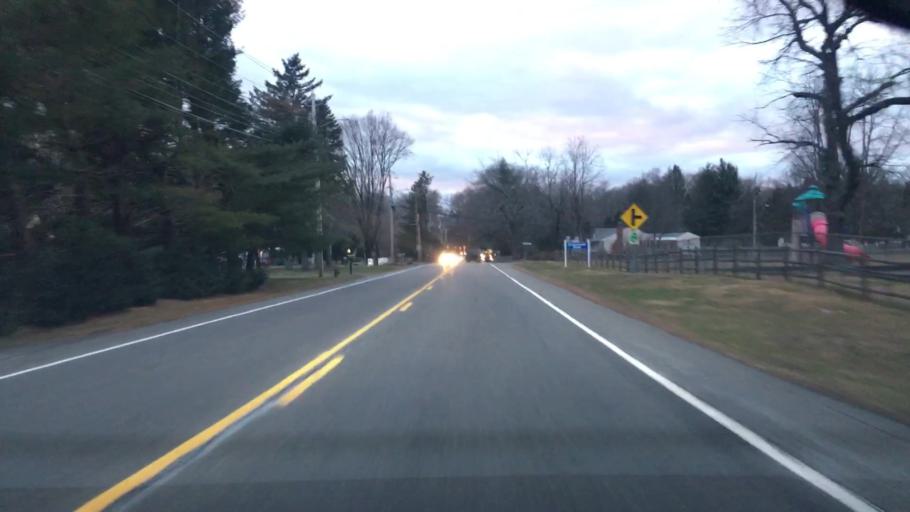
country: US
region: New York
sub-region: Dutchess County
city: Red Oaks Mill
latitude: 41.6683
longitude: -73.8805
